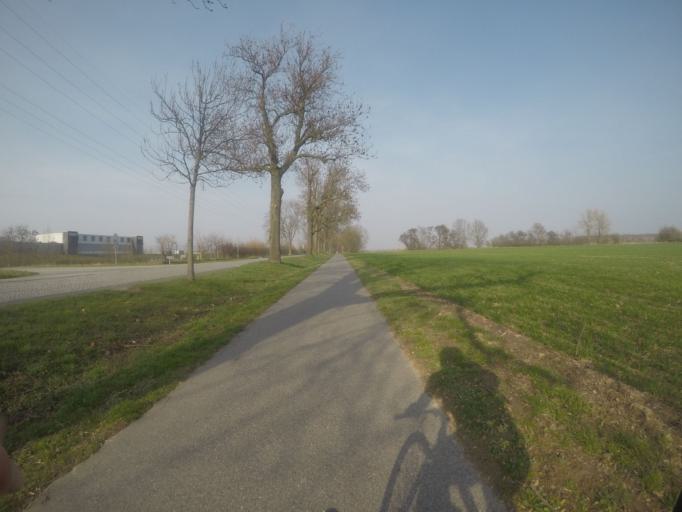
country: DE
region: Brandenburg
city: Schonefeld
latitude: 52.3810
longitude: 13.4732
